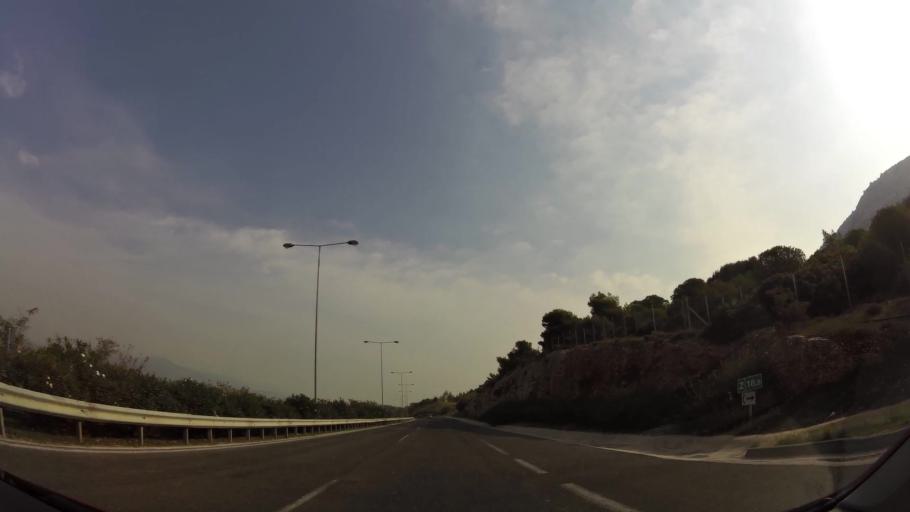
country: GR
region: Attica
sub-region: Nomarchia Athinas
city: Petroupolis
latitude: 38.0595
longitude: 23.6634
